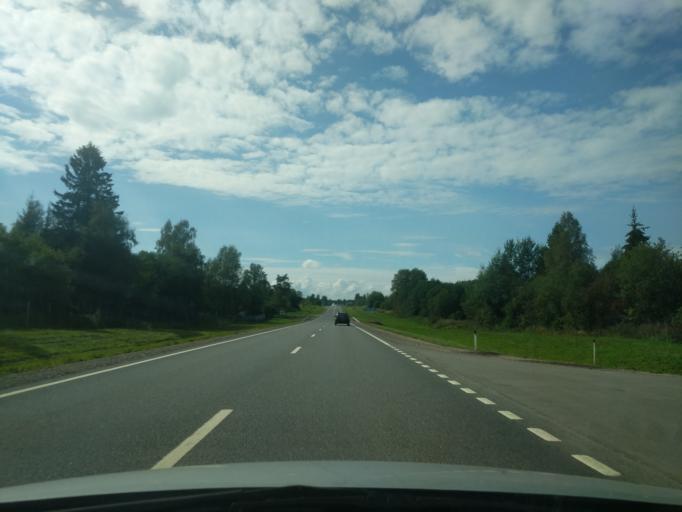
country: RU
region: Kostroma
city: Oktyabr'skiy
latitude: 57.7981
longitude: 41.2334
